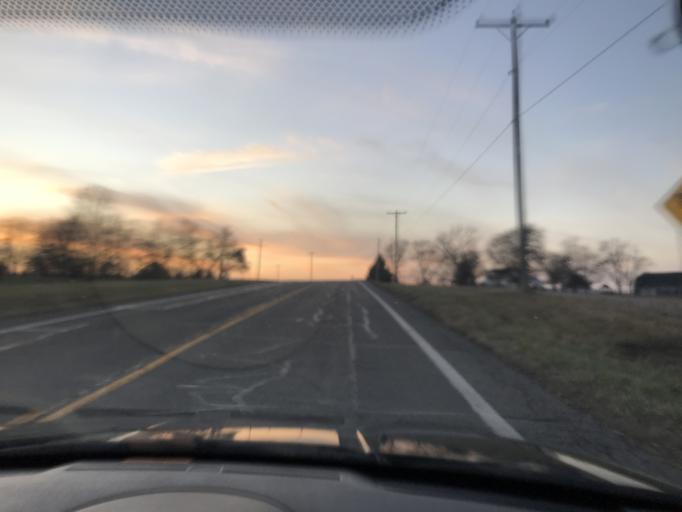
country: US
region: Ohio
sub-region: Champaign County
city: Urbana
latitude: 40.1086
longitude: -83.7010
